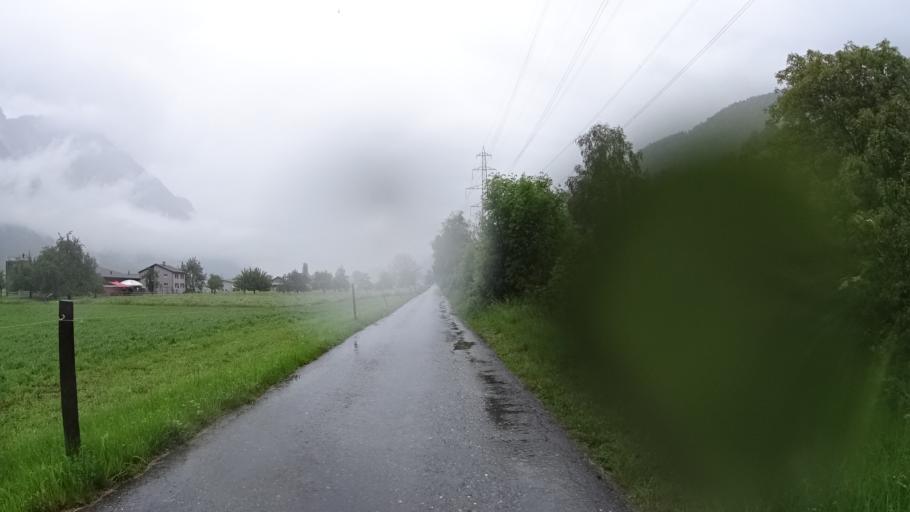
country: CH
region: Saint Gallen
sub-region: Wahlkreis Sarganserland
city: Flums
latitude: 47.0830
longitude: 9.3607
